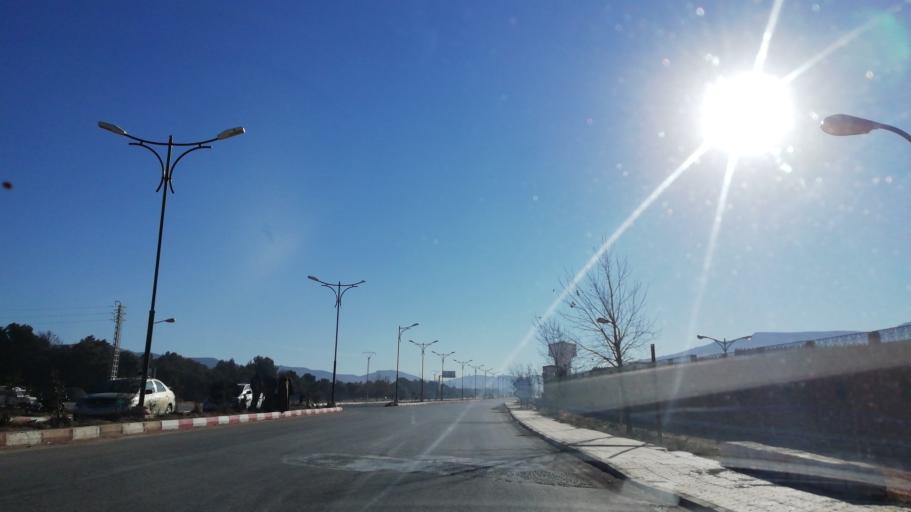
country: DZ
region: El Bayadh
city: El Bayadh
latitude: 33.6661
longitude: 1.0468
